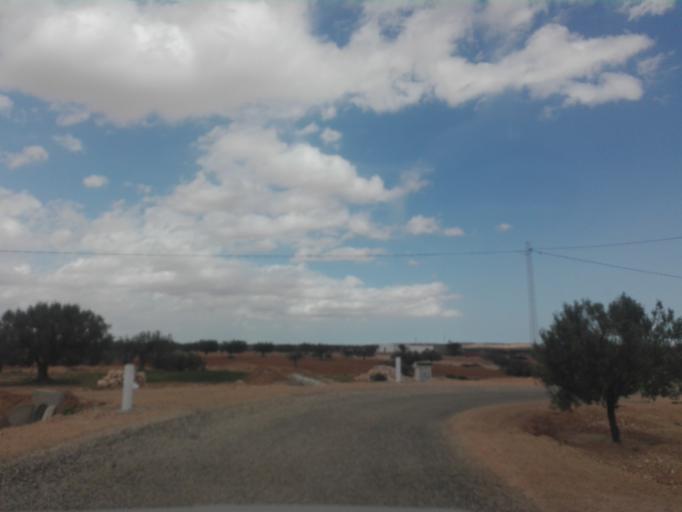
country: TN
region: Safaqis
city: Sfax
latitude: 34.6887
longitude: 10.4470
